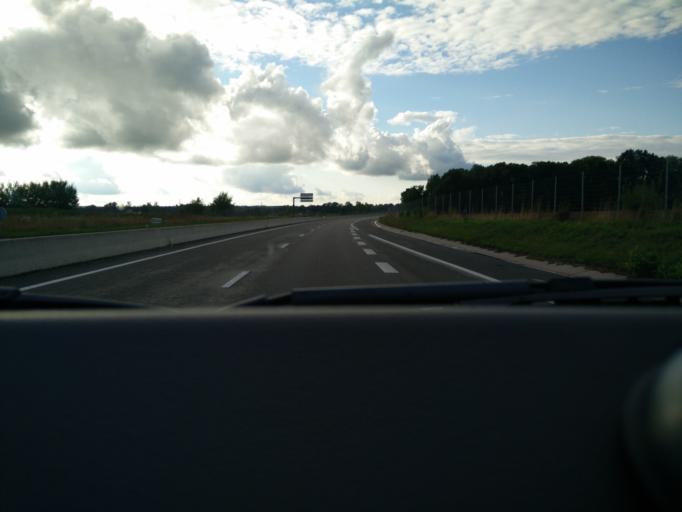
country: FR
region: Lorraine
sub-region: Departement de Meurthe-et-Moselle
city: Baccarat
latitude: 48.4683
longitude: 6.7317
